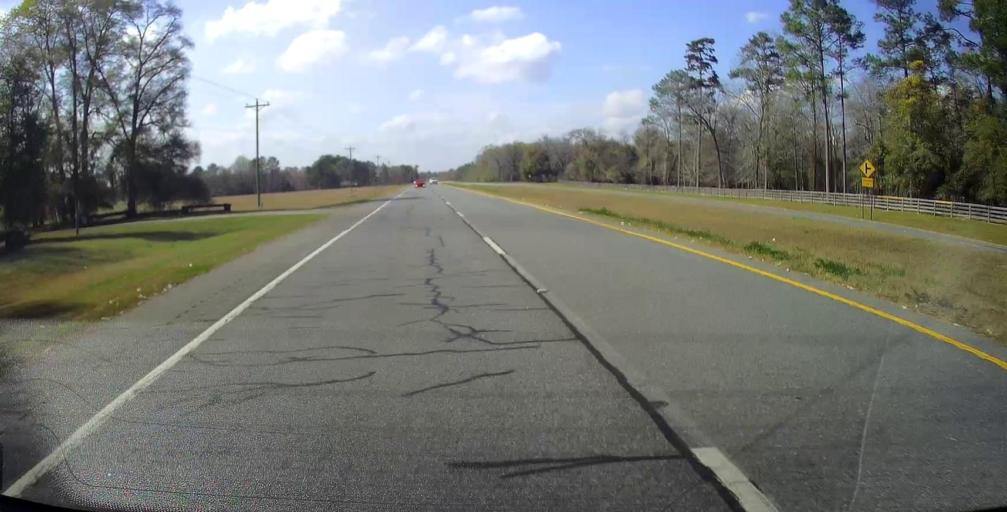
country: US
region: Georgia
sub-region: Pulaski County
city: Hawkinsville
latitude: 32.2721
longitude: -83.4189
